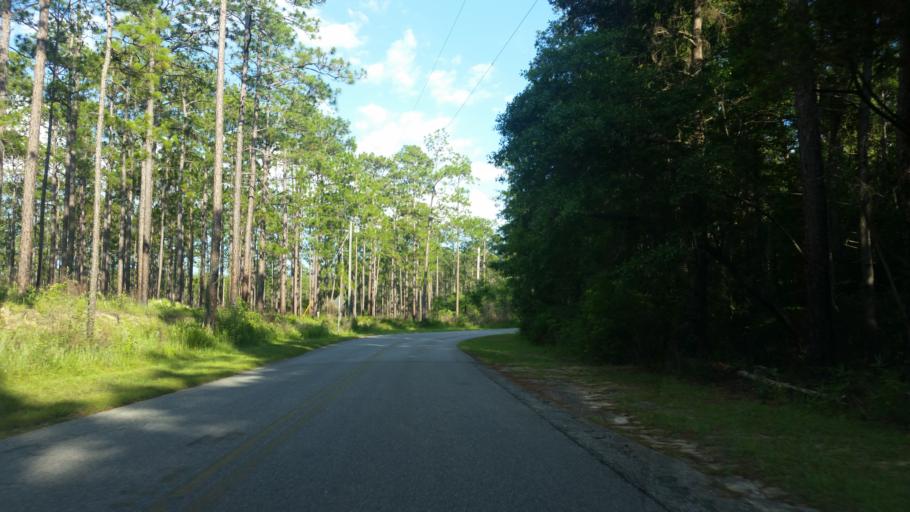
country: US
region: Florida
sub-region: Santa Rosa County
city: East Milton
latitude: 30.7038
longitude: -86.8802
